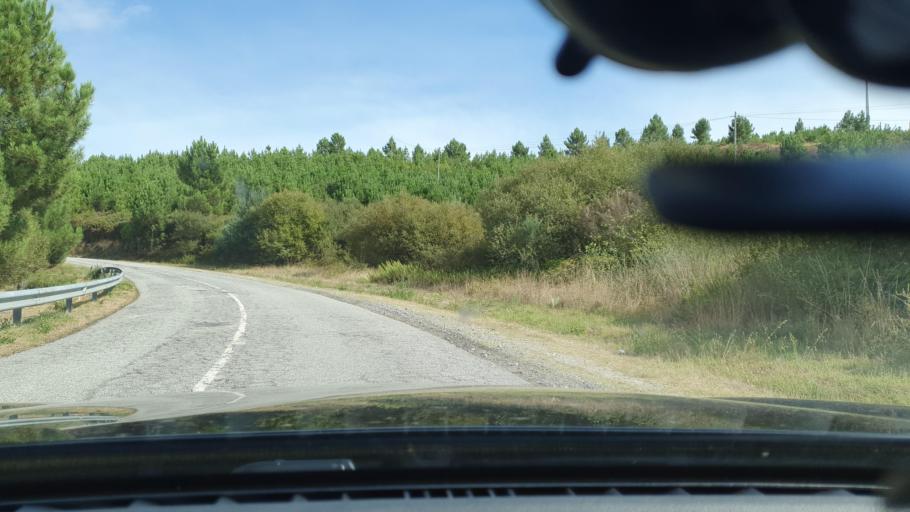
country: PT
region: Vila Real
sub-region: Chaves
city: Chaves
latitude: 41.7974
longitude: -7.5174
